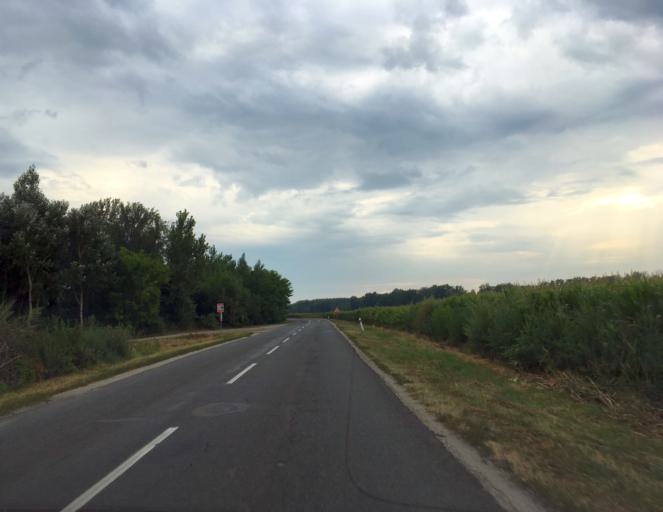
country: SK
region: Trnavsky
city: Gabcikovo
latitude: 47.8856
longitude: 17.6605
